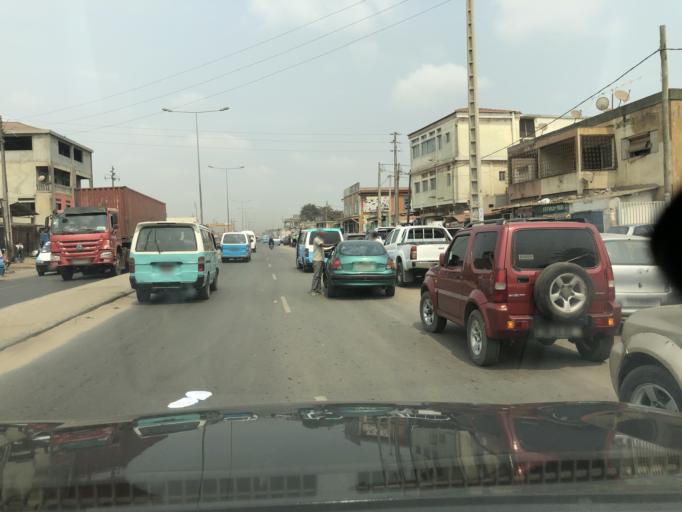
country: AO
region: Luanda
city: Luanda
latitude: -8.8012
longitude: 13.3109
